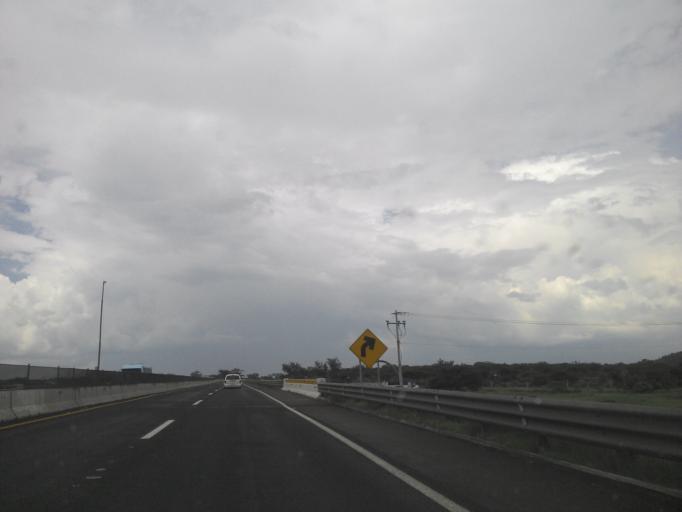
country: MX
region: Hidalgo
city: Tula de Allende
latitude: 20.0715
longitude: -99.3691
